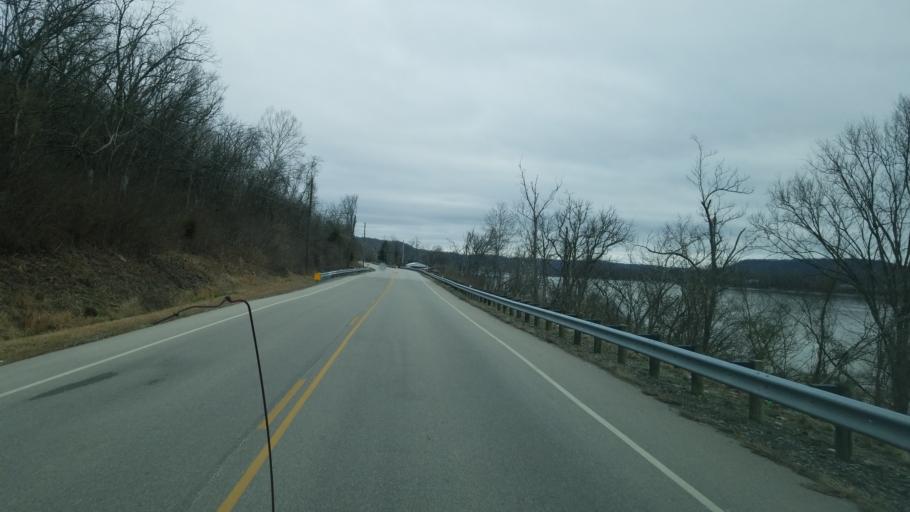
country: US
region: Ohio
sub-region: Brown County
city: Ripley
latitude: 38.7681
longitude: -83.8995
